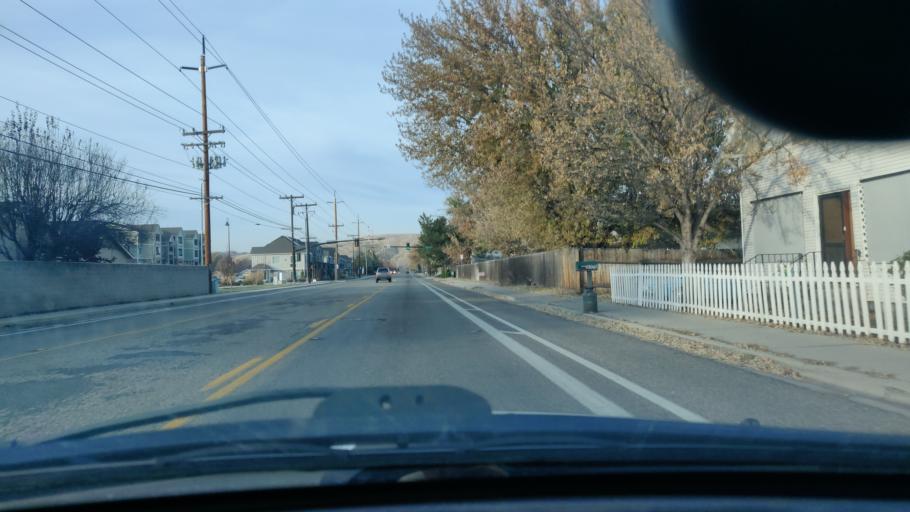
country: US
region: Idaho
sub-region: Ada County
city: Garden City
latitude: 43.6705
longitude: -116.2792
